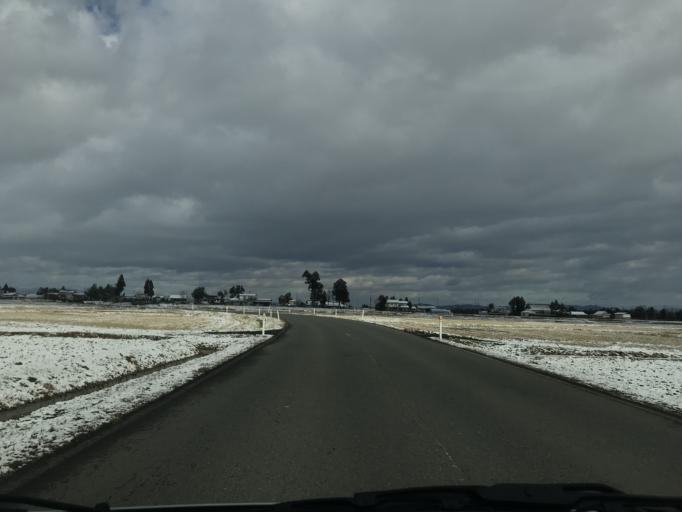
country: JP
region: Iwate
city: Mizusawa
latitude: 39.1553
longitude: 141.1135
